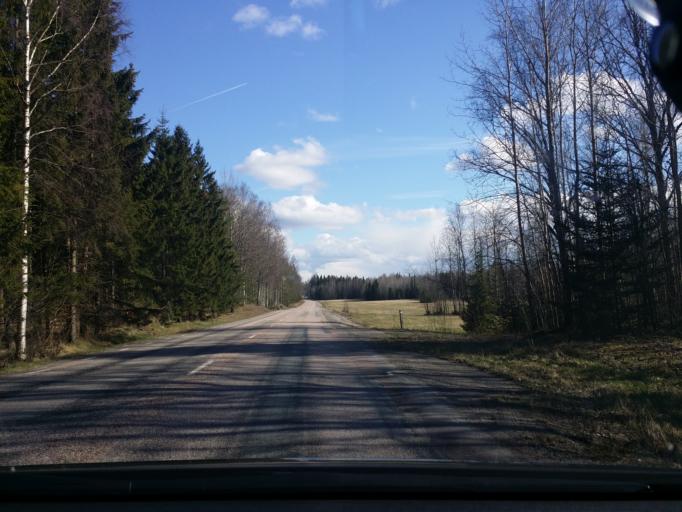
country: SE
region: Vaestmanland
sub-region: Sala Kommun
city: Sala
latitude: 59.9803
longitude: 16.4899
